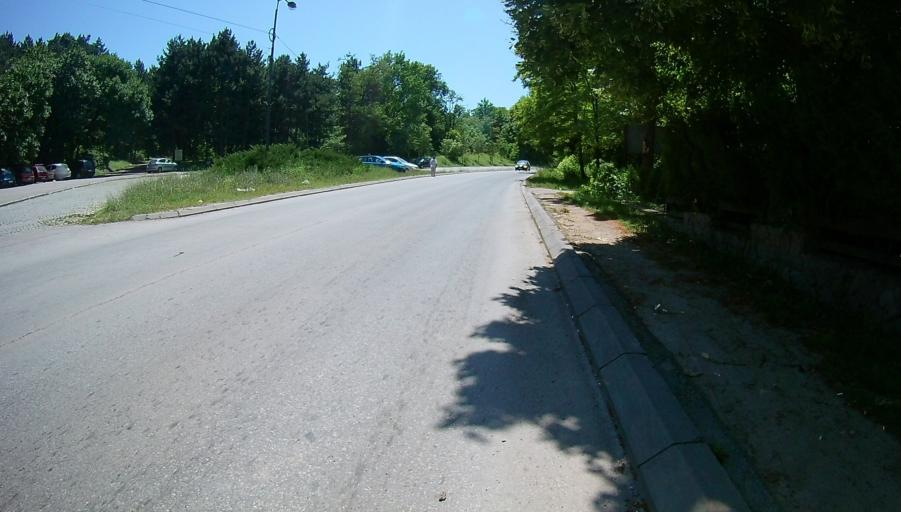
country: RS
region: Central Serbia
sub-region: Nisavski Okrug
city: Nis
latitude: 43.3074
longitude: 21.8686
